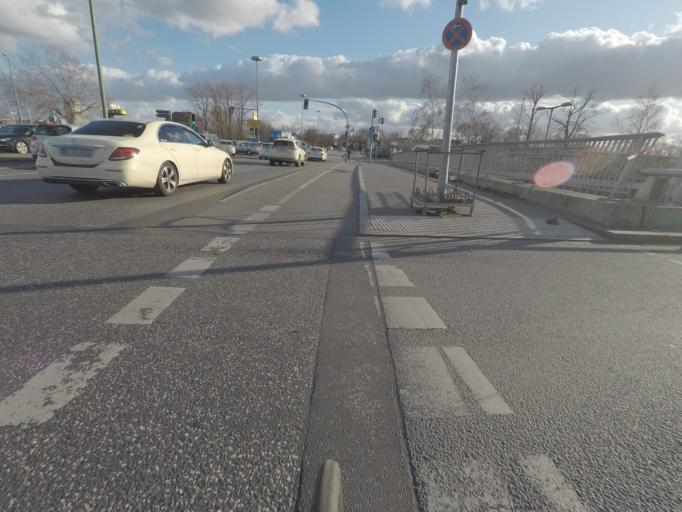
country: DE
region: Berlin
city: Moabit
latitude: 52.5383
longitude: 13.3259
